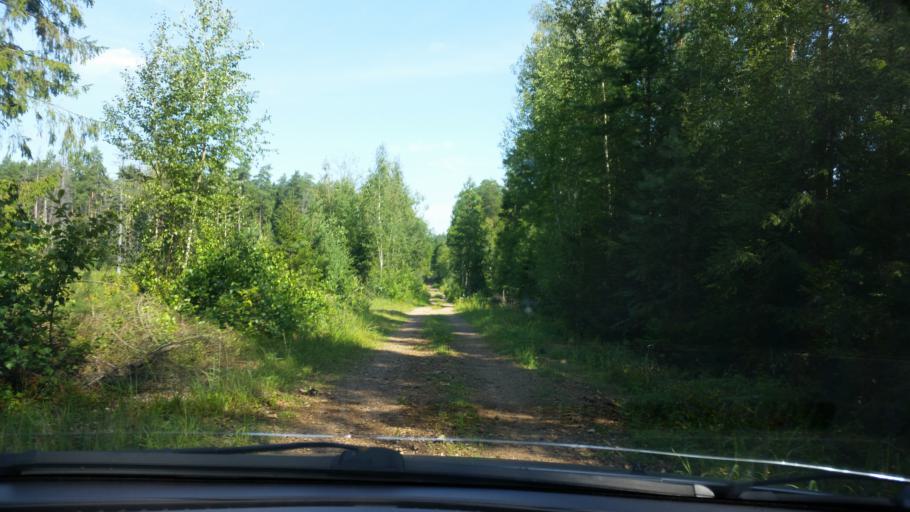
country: RU
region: Moskovskaya
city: Bol'shoye Gryzlovo
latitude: 54.8975
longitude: 37.7618
